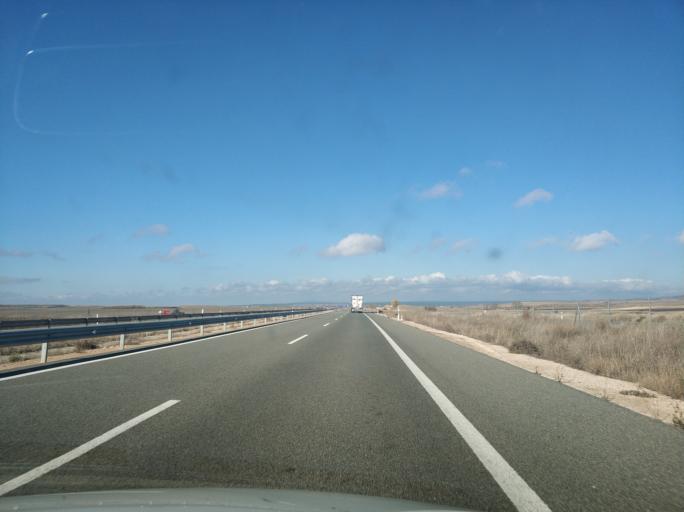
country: ES
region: Castille and Leon
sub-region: Provincia de Soria
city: Coscurita
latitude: 41.4023
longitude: -2.4783
